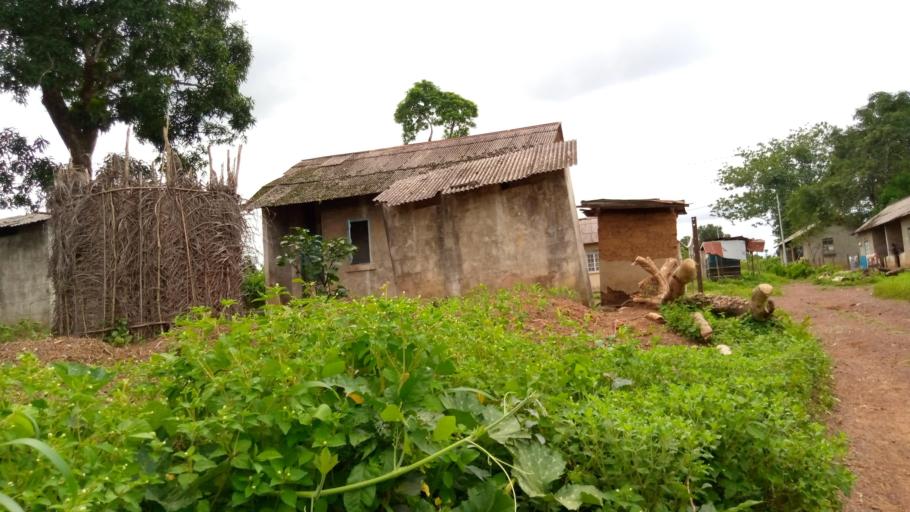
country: SL
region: Southern Province
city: Rotifunk
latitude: 8.1913
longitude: -12.5676
